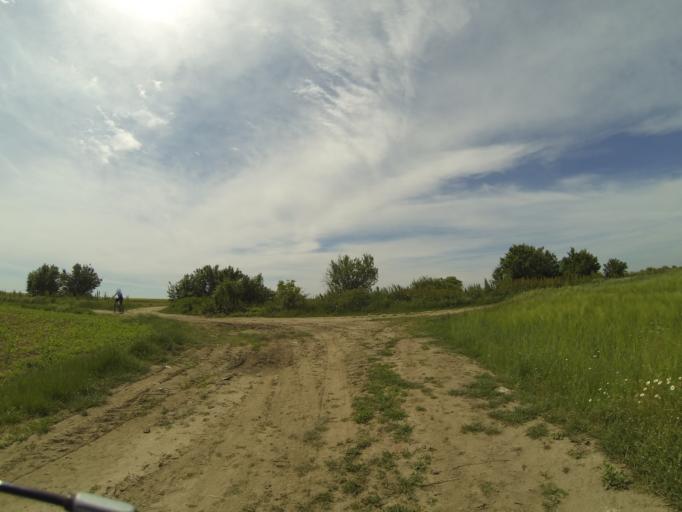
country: RO
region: Dolj
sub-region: Comuna Ghindeni
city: Ghindeni
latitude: 44.2077
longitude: 23.9385
